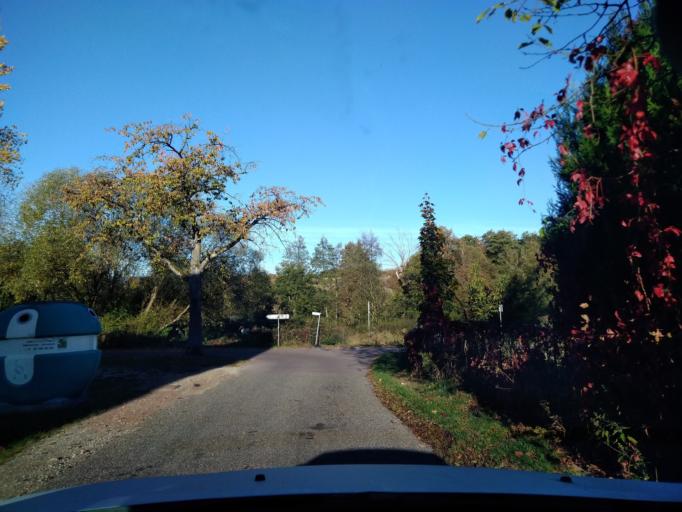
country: FR
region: Lorraine
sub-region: Departement de la Moselle
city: Sarreguemines
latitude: 49.1222
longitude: 7.0718
